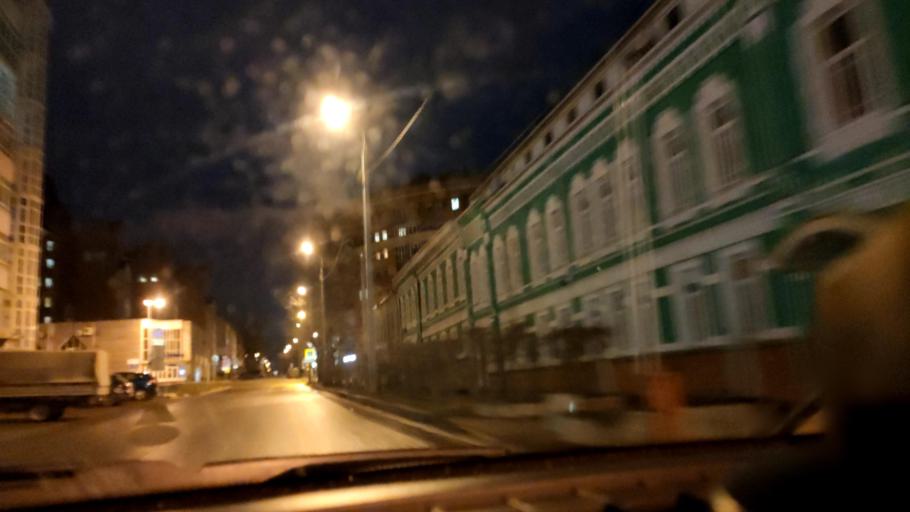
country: RU
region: Perm
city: Perm
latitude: 58.0186
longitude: 56.2514
